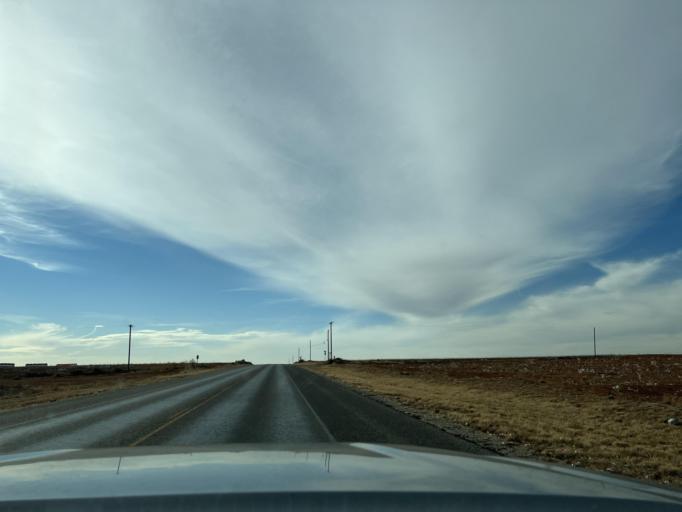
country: US
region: Texas
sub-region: Fisher County
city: Roby
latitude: 32.7416
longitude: -100.4548
